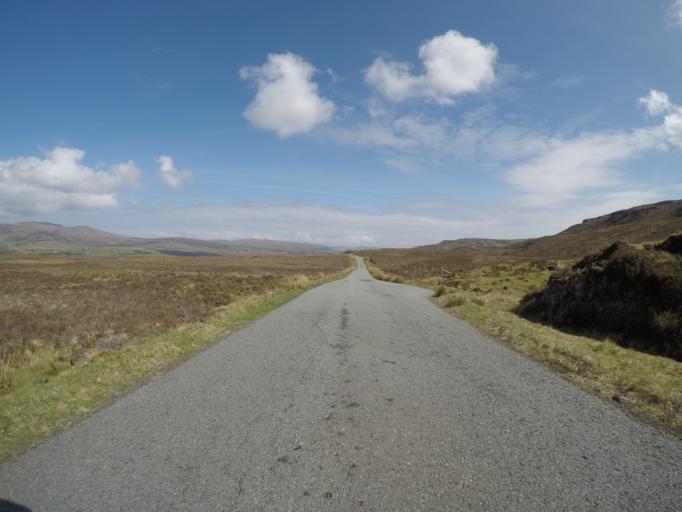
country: GB
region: Scotland
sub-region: Highland
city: Isle of Skye
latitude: 57.4227
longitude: -6.2746
